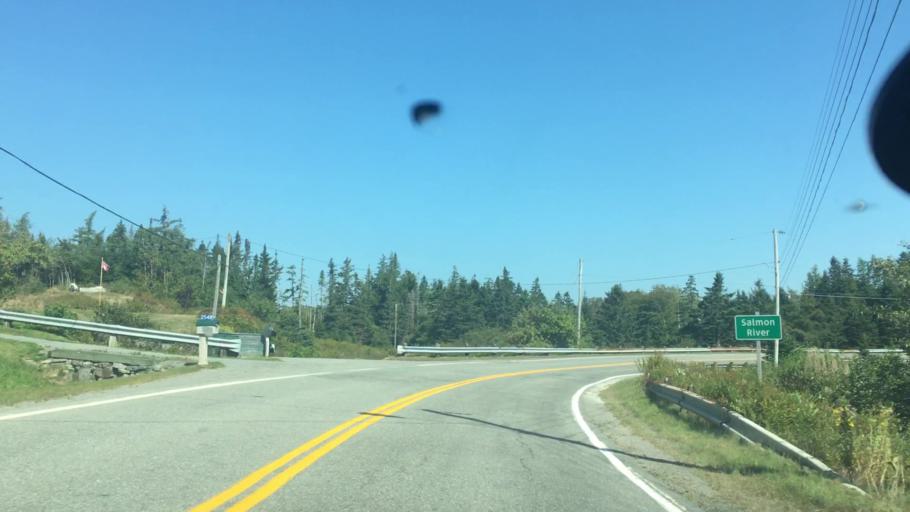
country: CA
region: Nova Scotia
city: New Glasgow
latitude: 44.9159
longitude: -62.3846
